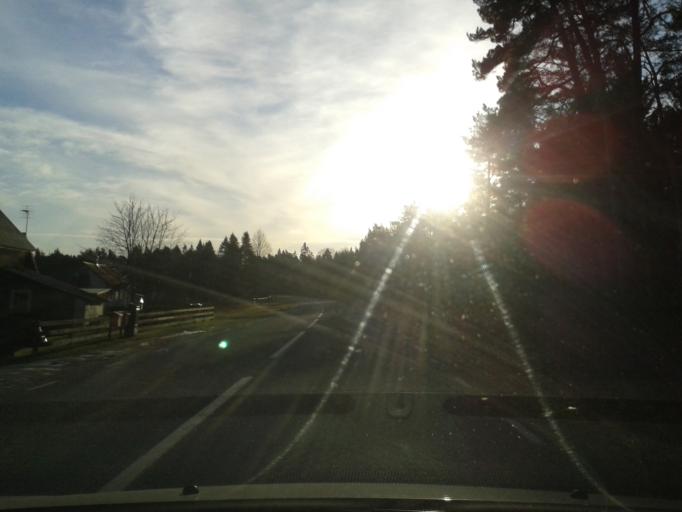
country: SE
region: Gotland
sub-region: Gotland
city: Hemse
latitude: 57.3570
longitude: 18.6855
